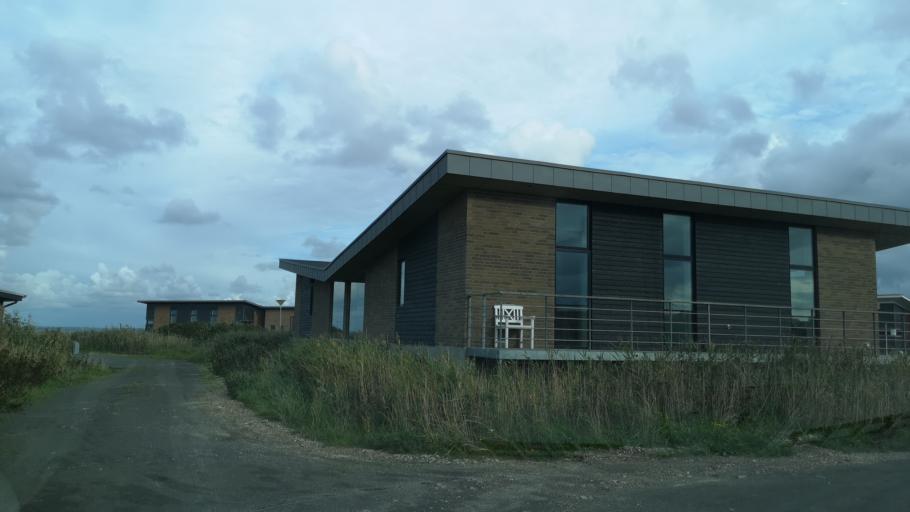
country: DK
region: Central Jutland
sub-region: Ringkobing-Skjern Kommune
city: Hvide Sande
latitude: 56.0099
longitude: 8.1321
